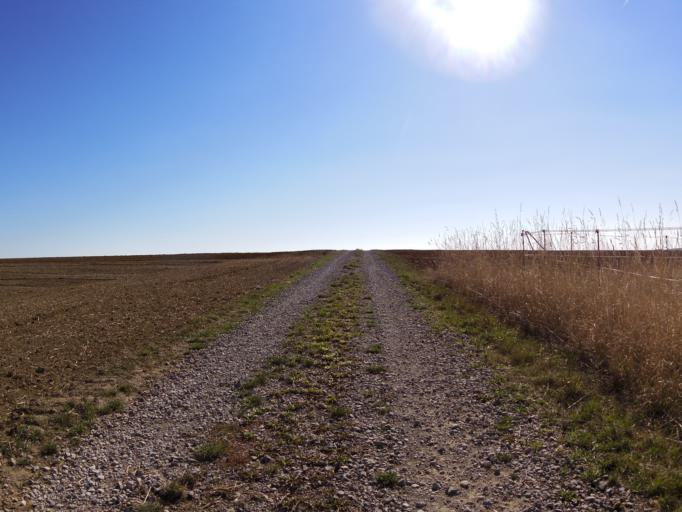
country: DE
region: Bavaria
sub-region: Regierungsbezirk Unterfranken
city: Reichenberg
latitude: 49.7345
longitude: 9.9285
